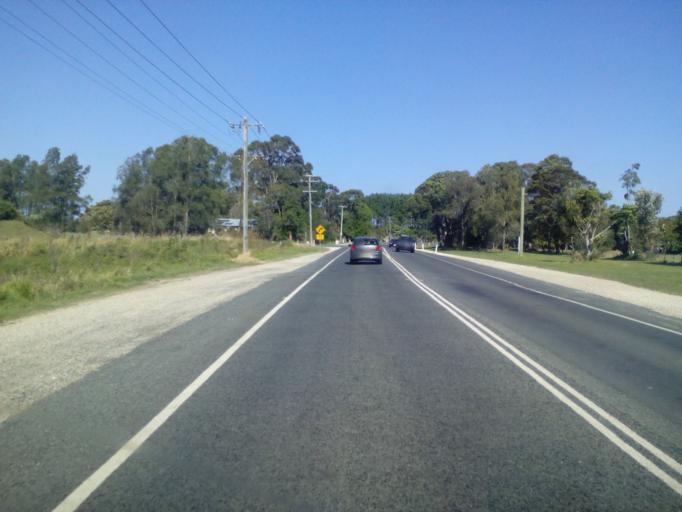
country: AU
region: New South Wales
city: Chinderah
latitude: -28.2511
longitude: 153.5574
